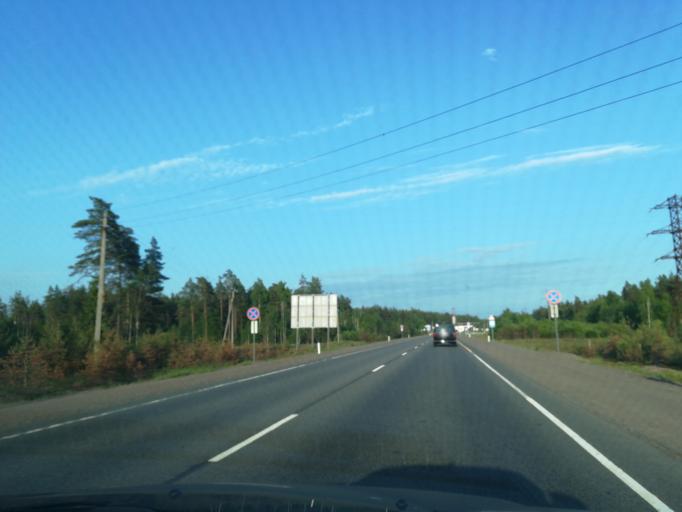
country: RU
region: Leningrad
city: Vyborg
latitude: 60.6660
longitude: 28.9228
